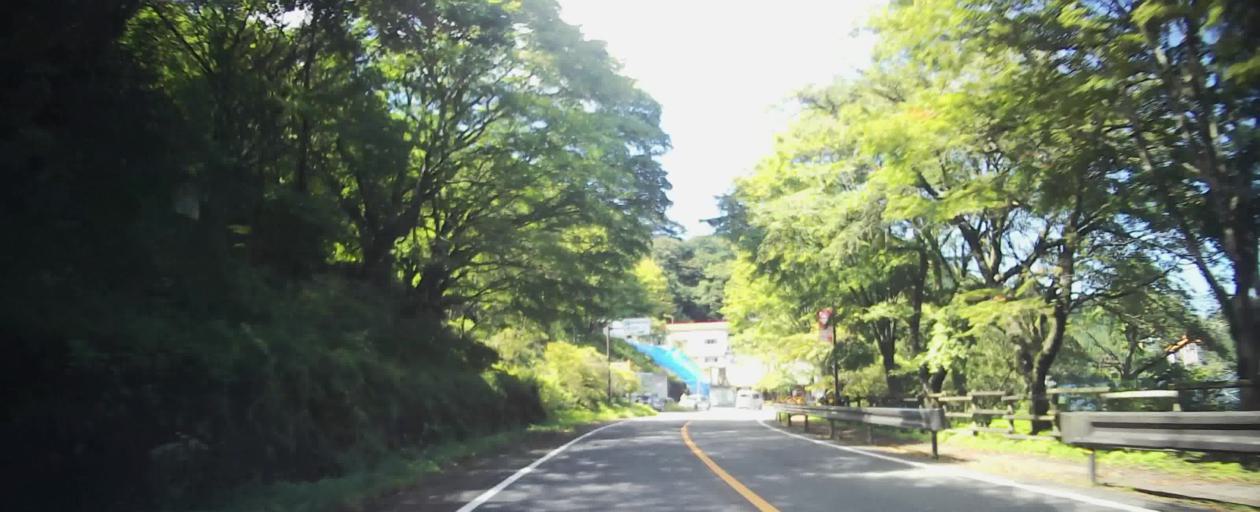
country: JP
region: Gunma
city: Nakanojomachi
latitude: 36.4689
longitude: 138.8659
